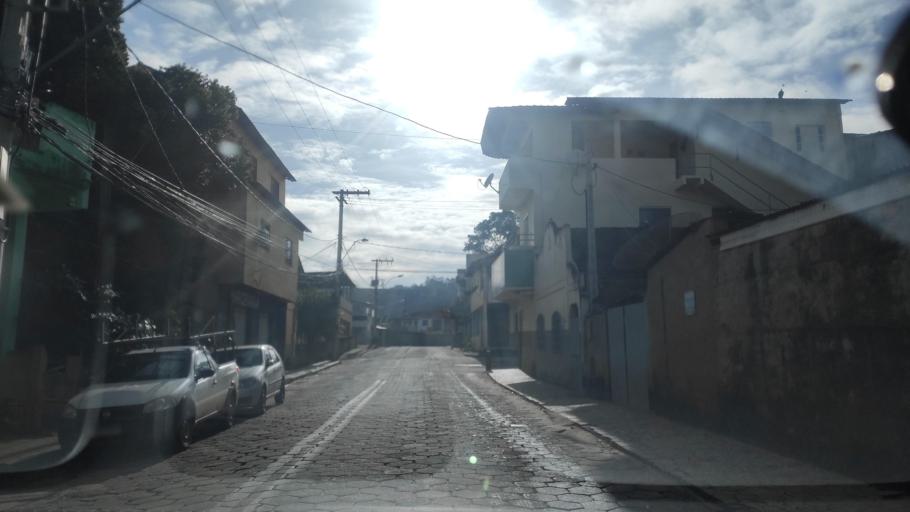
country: BR
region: Espirito Santo
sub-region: Nova Venecia
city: Nova Venecia
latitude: -18.7131
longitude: -40.3923
